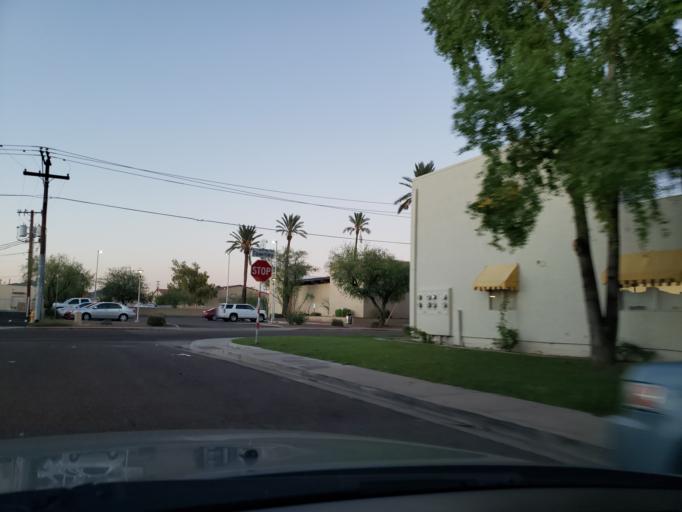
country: US
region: Arizona
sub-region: Maricopa County
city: Phoenix
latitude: 33.5657
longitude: -112.0636
